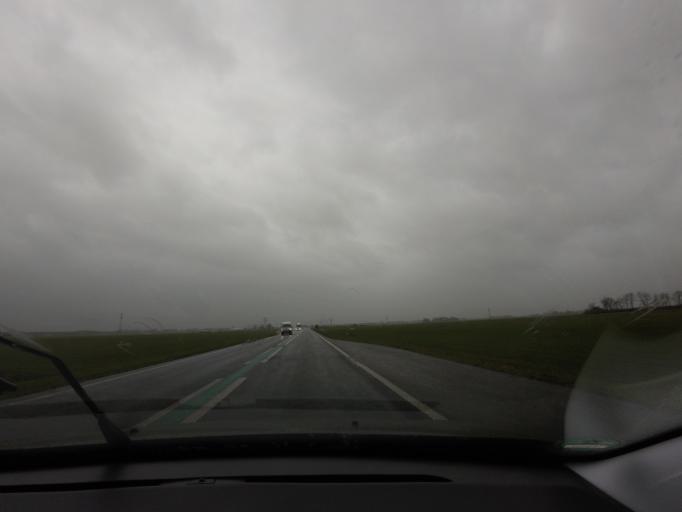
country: NL
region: Friesland
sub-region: Sudwest Fryslan
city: Bolsward
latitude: 53.0809
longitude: 5.5182
